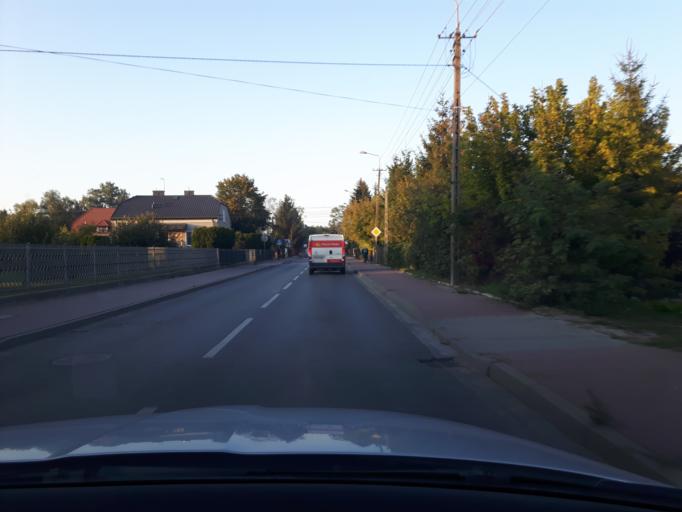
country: PL
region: Masovian Voivodeship
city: Zielonka
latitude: 52.3291
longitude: 21.1702
